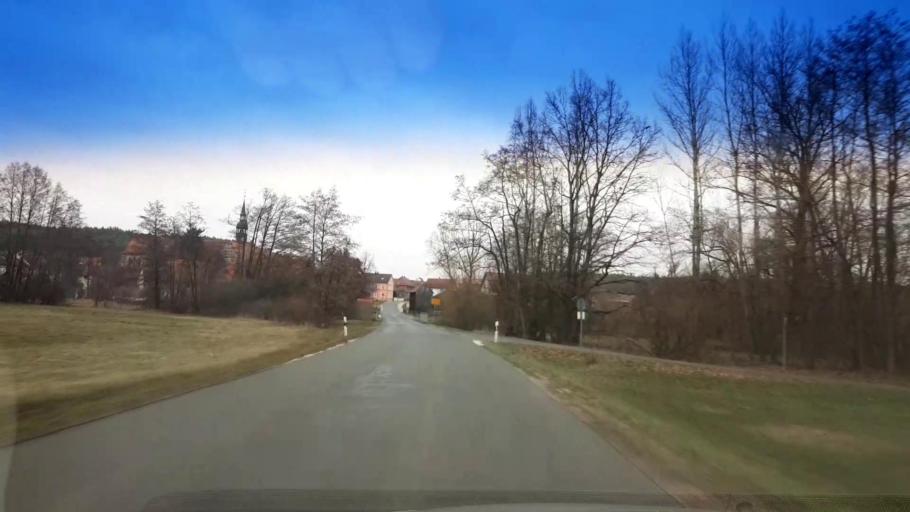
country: DE
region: Bavaria
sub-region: Upper Franconia
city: Pettstadt
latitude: 49.7922
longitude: 10.9063
